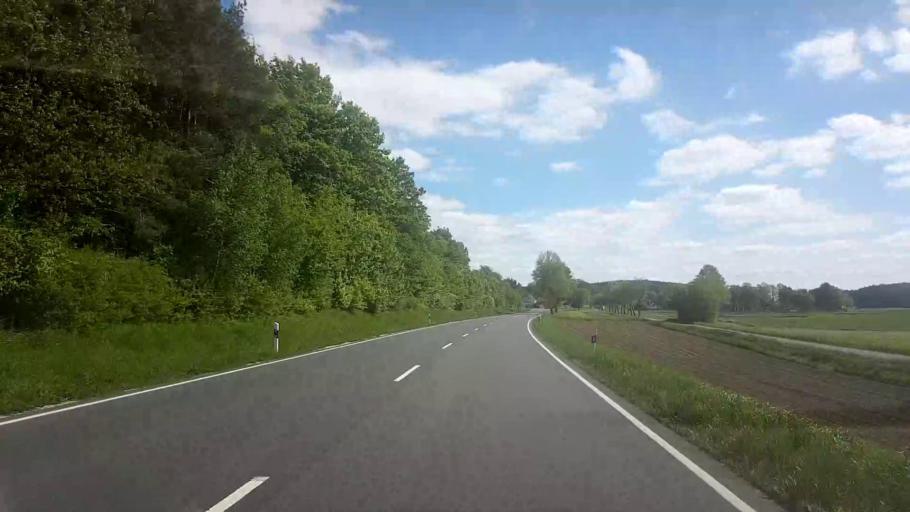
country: DE
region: Bavaria
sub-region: Upper Franconia
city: Rattelsdorf
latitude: 50.0515
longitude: 10.8798
